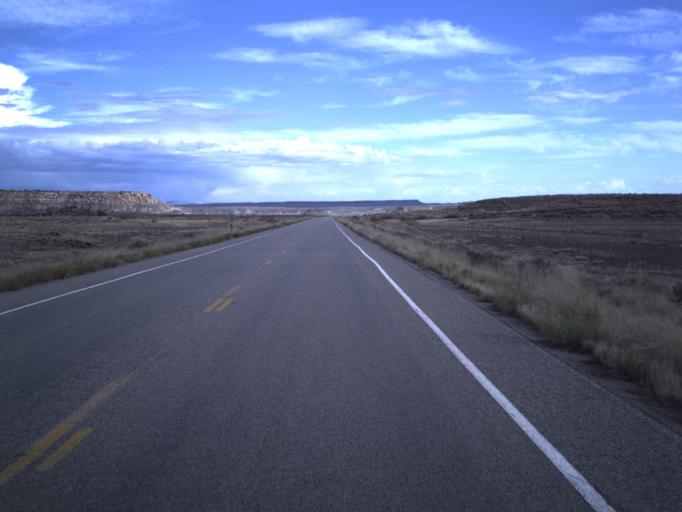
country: US
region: Colorado
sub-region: Montezuma County
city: Towaoc
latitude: 37.1695
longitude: -109.0864
